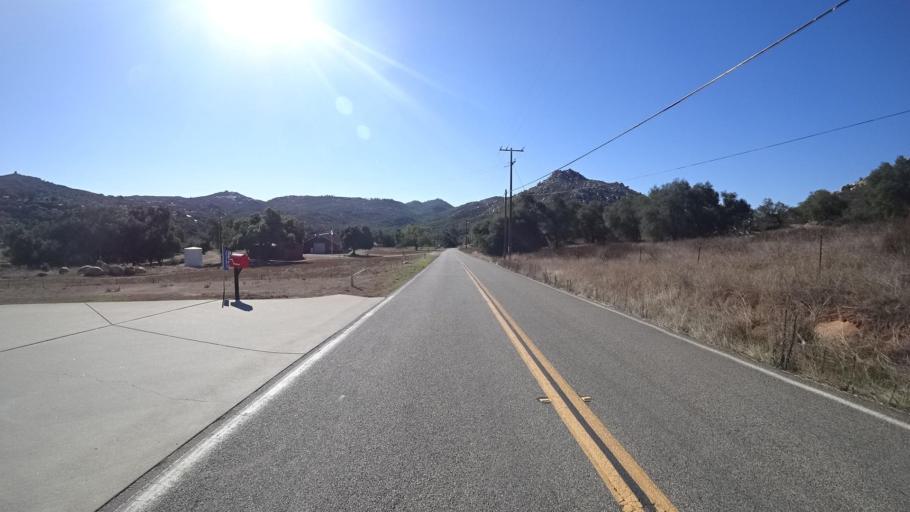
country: US
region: California
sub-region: San Diego County
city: Jamul
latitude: 32.6823
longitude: -116.7540
